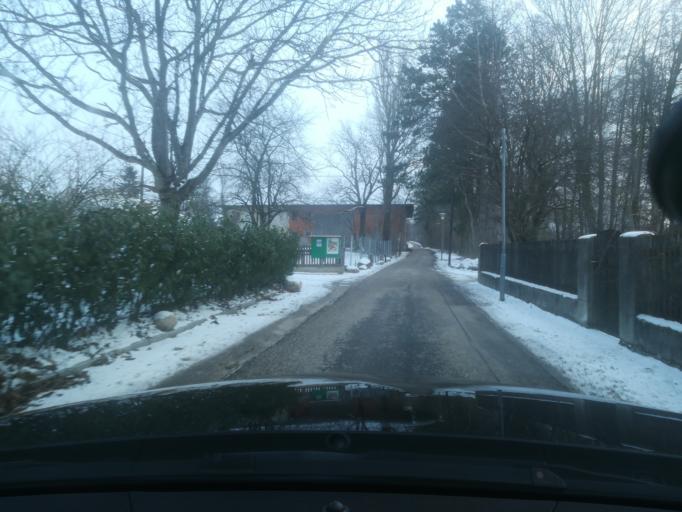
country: AT
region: Upper Austria
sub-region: Wels-Land
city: Marchtrenk
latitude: 48.1911
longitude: 14.1366
